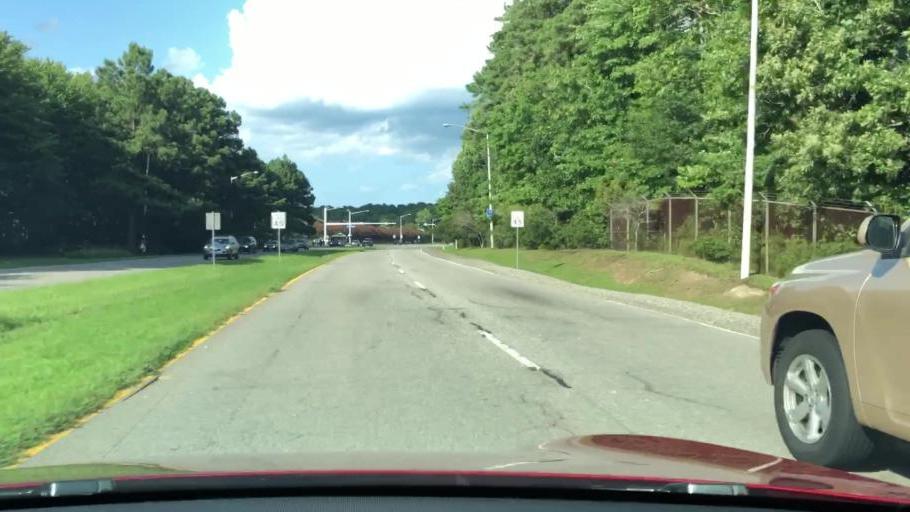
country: US
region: Virginia
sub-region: City of Virginia Beach
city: Virginia Beach
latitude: 36.8191
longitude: -75.9841
